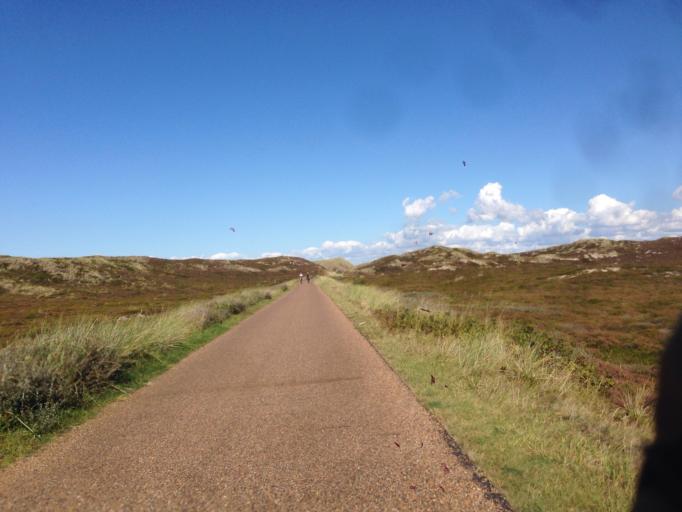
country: DE
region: Schleswig-Holstein
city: List
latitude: 54.9979
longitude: 8.3629
